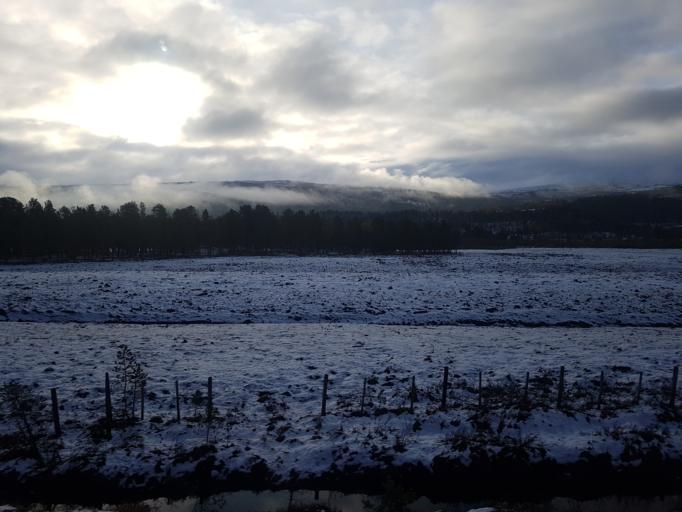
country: NO
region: Sor-Trondelag
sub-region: Oppdal
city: Oppdal
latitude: 62.6354
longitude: 9.7988
